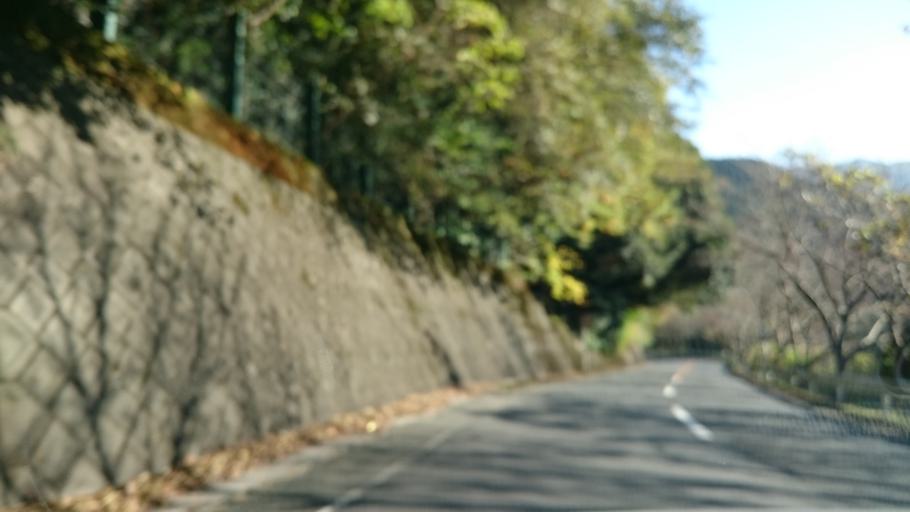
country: JP
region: Shizuoka
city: Heda
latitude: 34.9758
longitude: 138.8157
